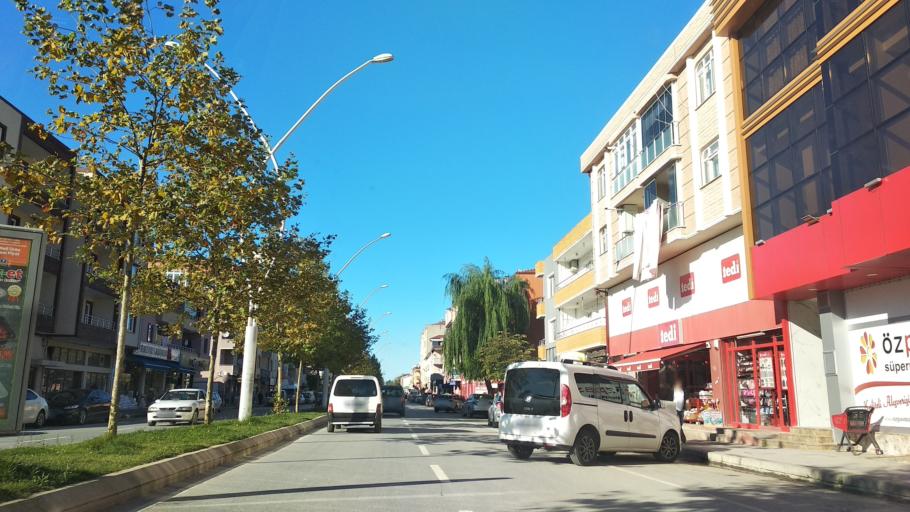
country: TR
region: Sakarya
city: Karasu
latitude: 41.1001
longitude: 30.6926
